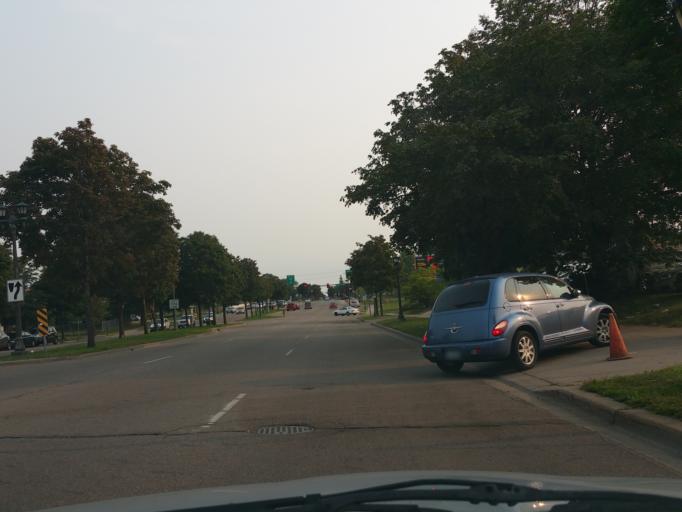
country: US
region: Minnesota
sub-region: Ramsey County
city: Falcon Heights
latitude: 44.9540
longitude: -93.1469
